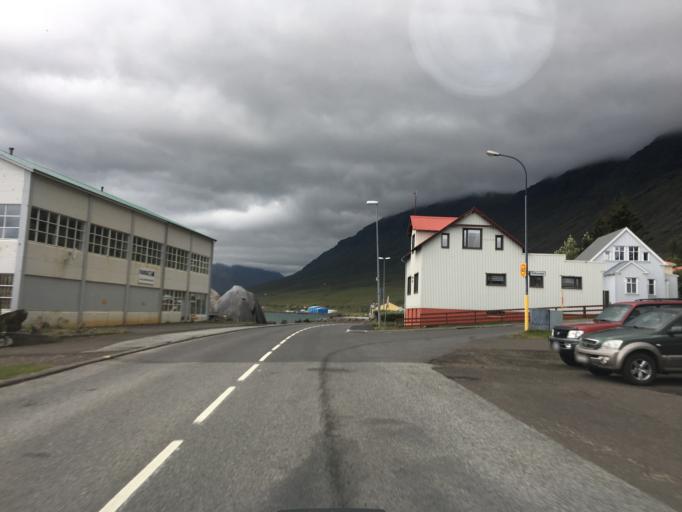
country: IS
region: East
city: Neskaupstadur
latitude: 65.1475
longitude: -13.7036
